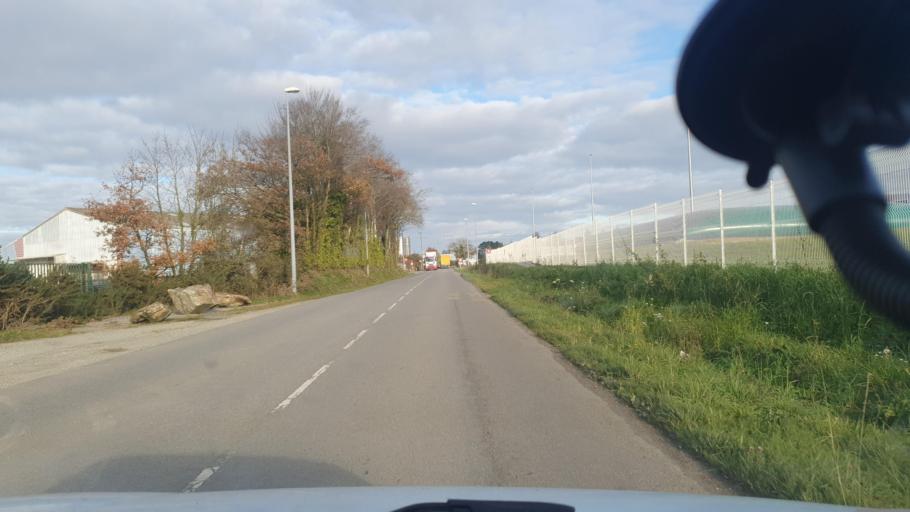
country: FR
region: Brittany
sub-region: Departement du Finistere
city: Briec
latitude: 48.0981
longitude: -4.0196
